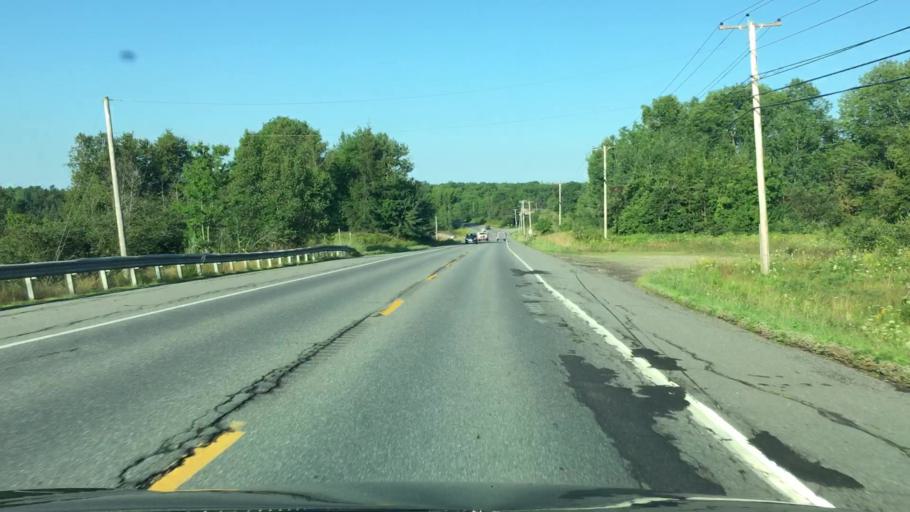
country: US
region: Maine
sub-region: Waldo County
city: Stockton Springs
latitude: 44.4708
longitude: -68.8936
